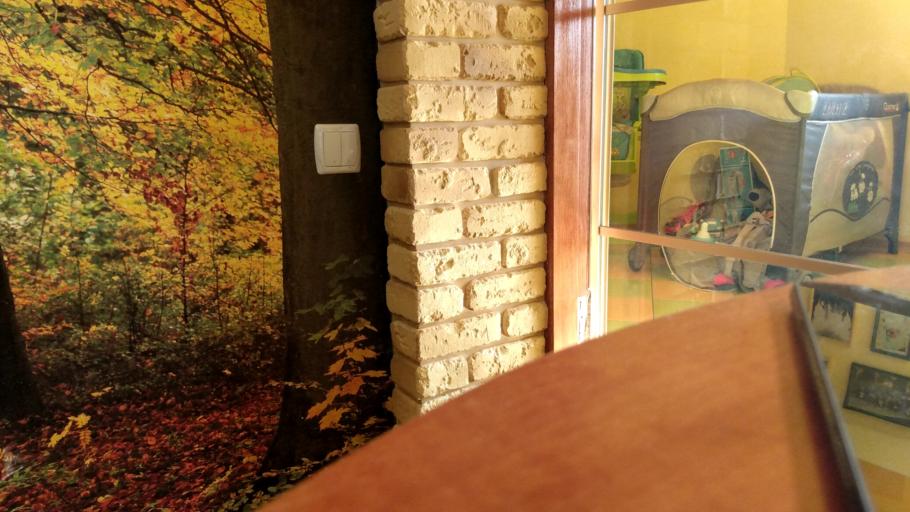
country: RU
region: Tverskaya
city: Radchenko
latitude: 56.7092
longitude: 36.4038
